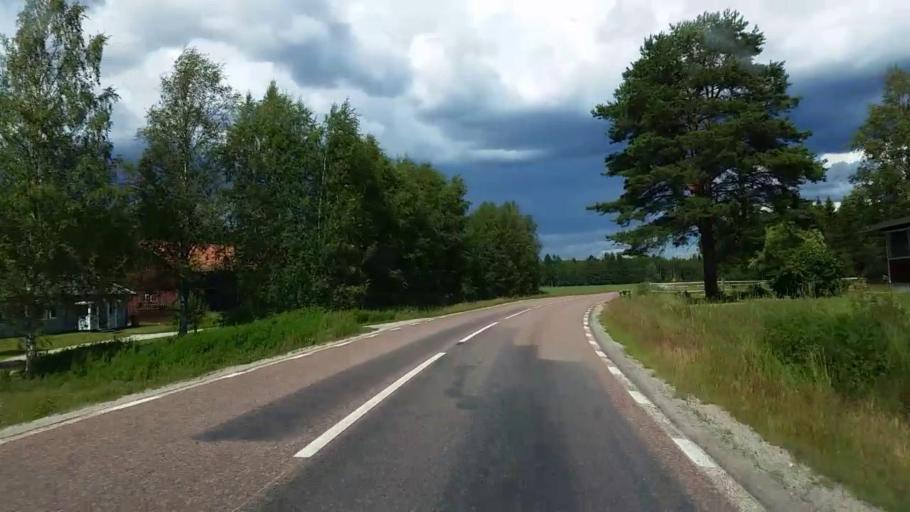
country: SE
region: Gaevleborg
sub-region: Ovanakers Kommun
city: Edsbyn
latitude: 61.3383
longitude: 15.5423
